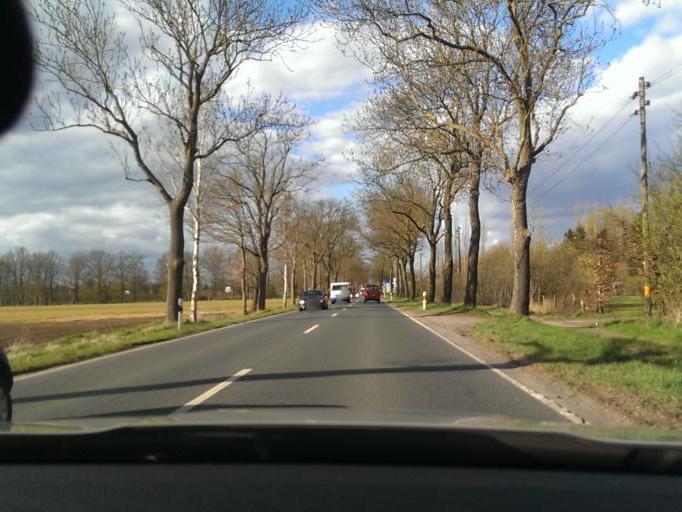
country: DE
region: Lower Saxony
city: Elze
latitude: 52.5740
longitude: 9.7273
